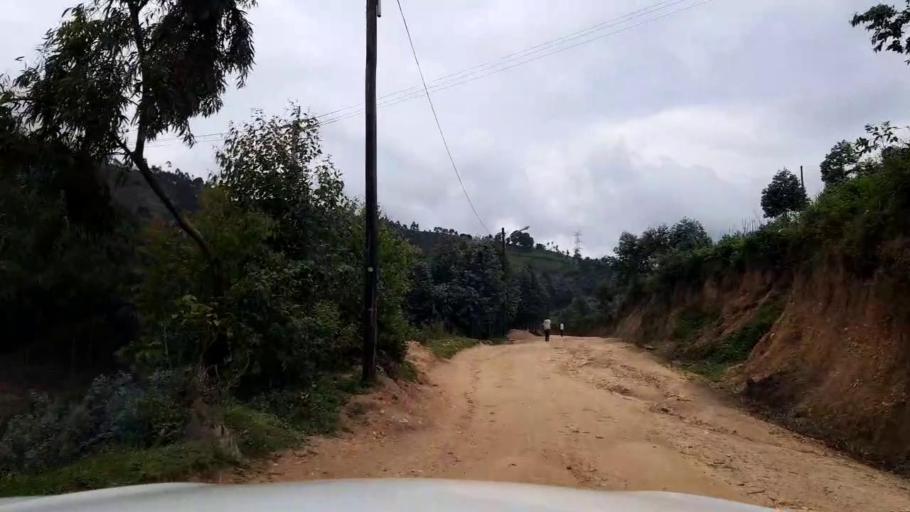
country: RW
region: Western Province
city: Kibuye
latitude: -1.9674
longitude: 29.3931
